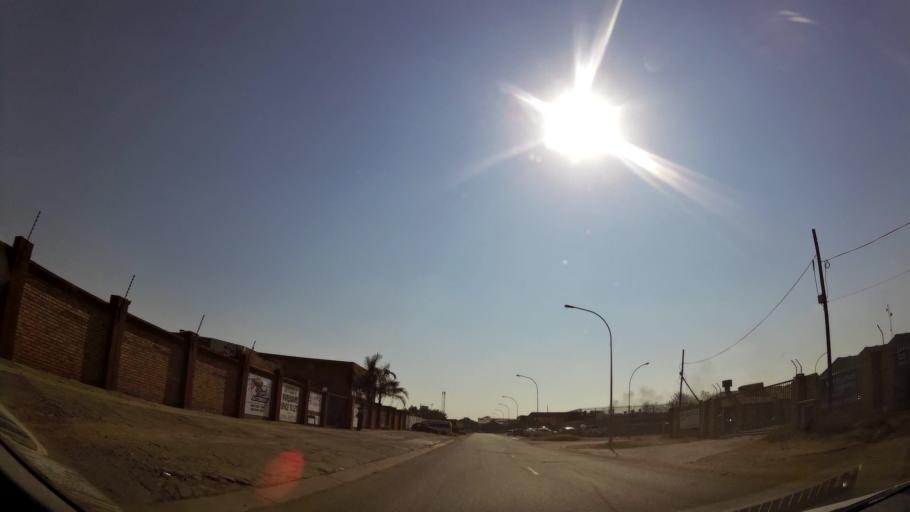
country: ZA
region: Gauteng
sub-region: Ekurhuleni Metropolitan Municipality
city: Benoni
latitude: -26.2070
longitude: 28.3028
